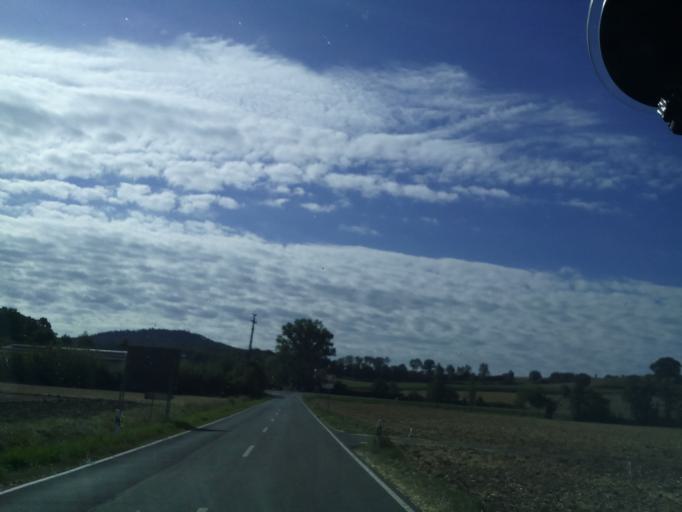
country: DE
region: Bavaria
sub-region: Upper Franconia
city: Buttenheim
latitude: 49.8046
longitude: 11.0416
